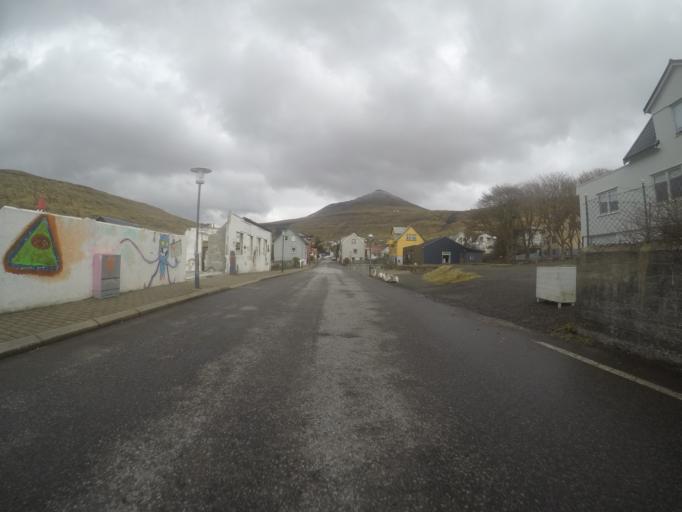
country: FO
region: Vagar
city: Midvagur
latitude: 62.0530
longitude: -7.1502
